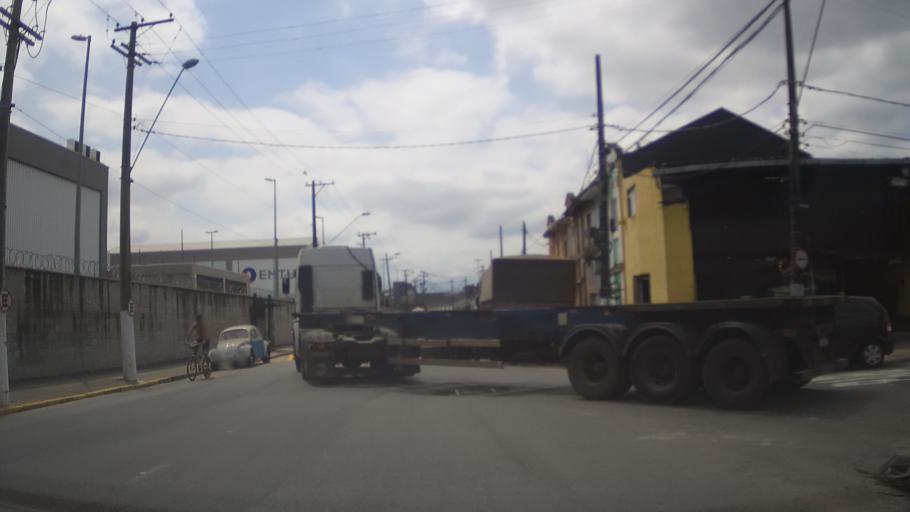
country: BR
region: Sao Paulo
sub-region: Santos
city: Santos
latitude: -23.9542
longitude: -46.3131
